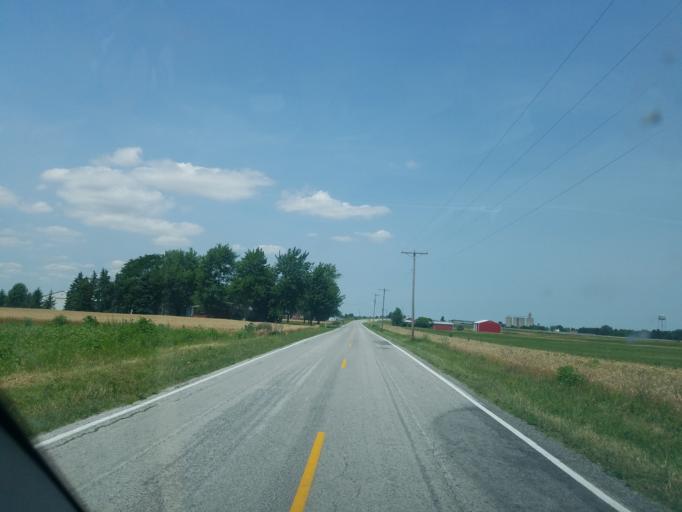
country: US
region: Ohio
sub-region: Wyandot County
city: Carey
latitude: 40.9640
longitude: -83.4860
